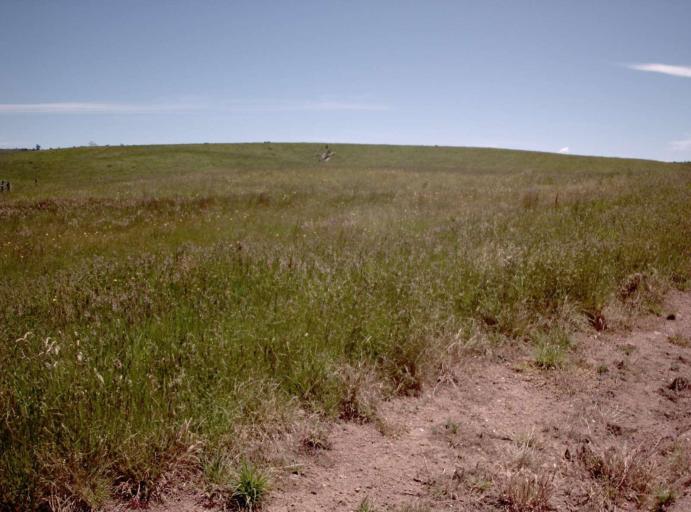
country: AU
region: New South Wales
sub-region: Snowy River
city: Jindabyne
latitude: -37.0987
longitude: 148.2526
